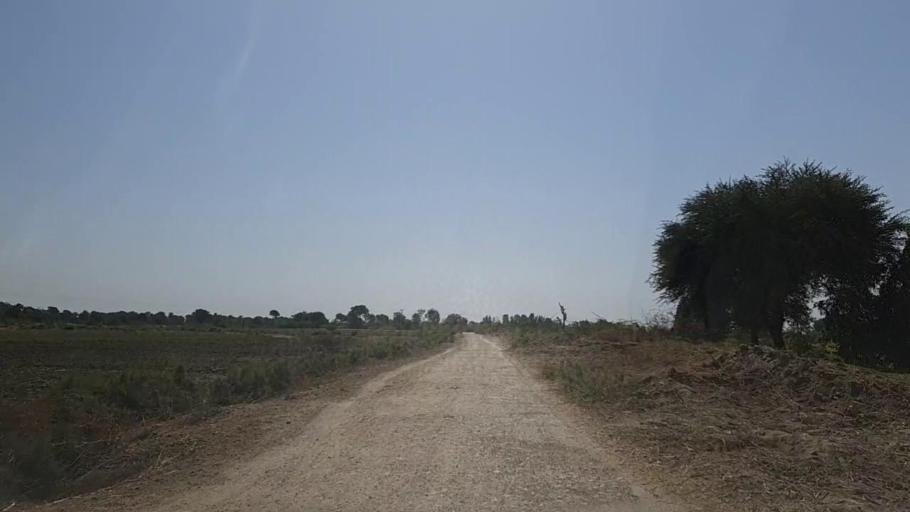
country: PK
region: Sindh
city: Samaro
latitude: 25.2460
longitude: 69.4109
